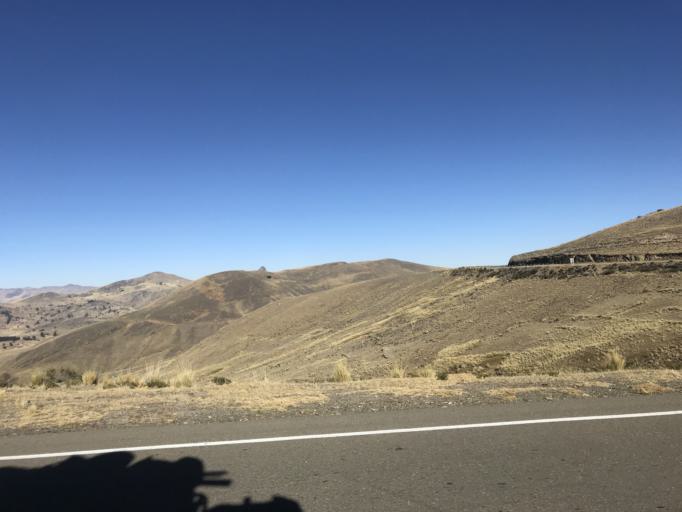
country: PE
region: Puno
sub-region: Yunguyo
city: Yunguyo
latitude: -16.1549
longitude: -68.9952
